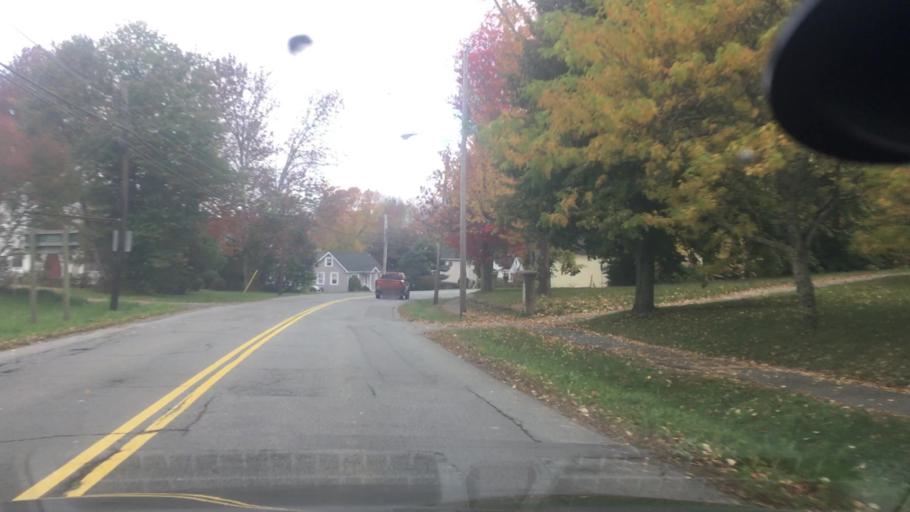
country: CA
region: Nova Scotia
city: Windsor
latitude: 44.9786
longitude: -64.1272
